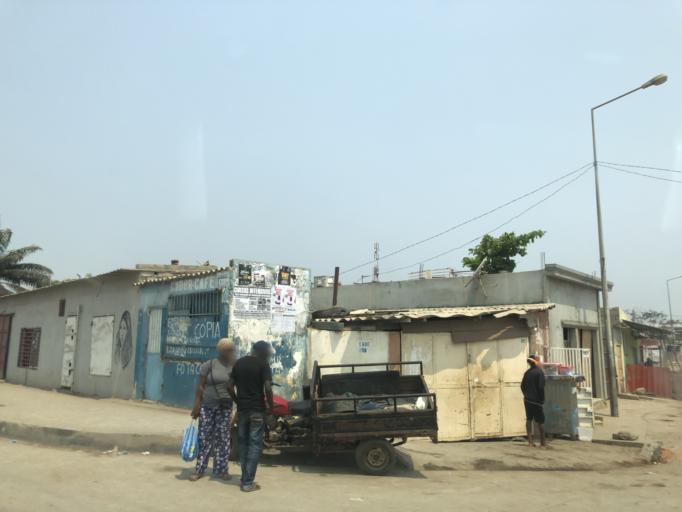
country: AO
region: Luanda
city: Luanda
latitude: -8.8486
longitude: 13.2069
